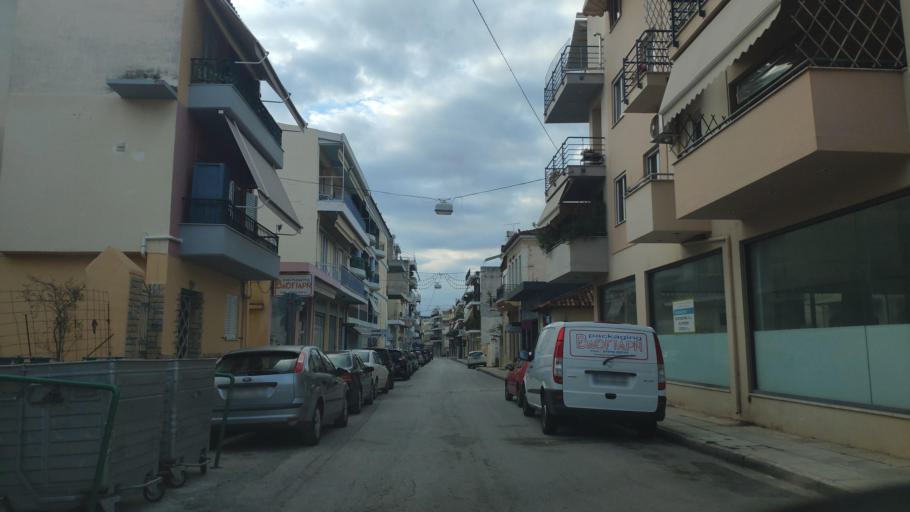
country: GR
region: Peloponnese
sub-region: Nomos Argolidos
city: Argos
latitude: 37.6406
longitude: 22.7292
